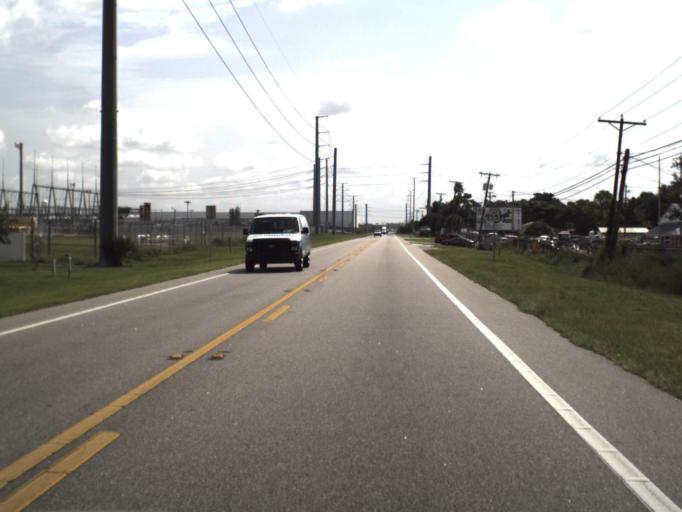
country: US
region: Florida
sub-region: Polk County
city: Auburndale
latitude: 28.0514
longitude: -81.8097
